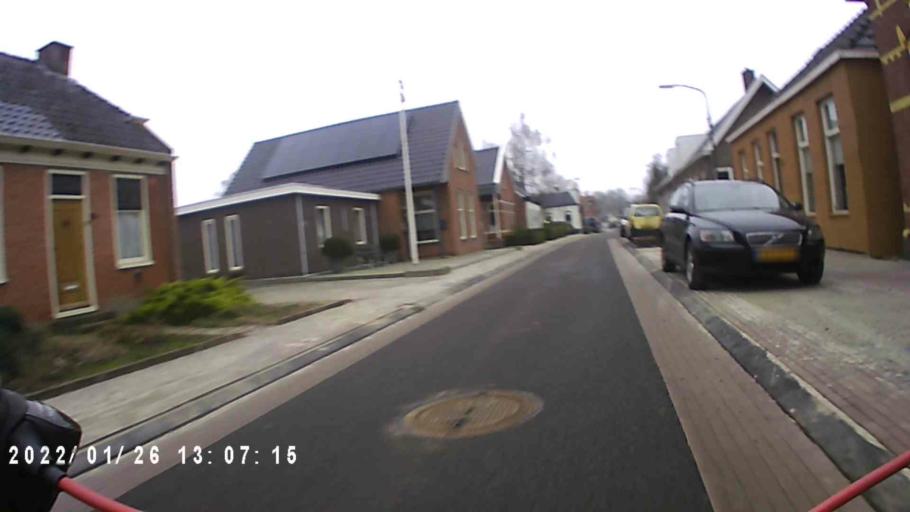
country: NL
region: Groningen
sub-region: Gemeente Zuidhorn
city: Oldehove
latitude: 53.3565
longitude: 6.4313
